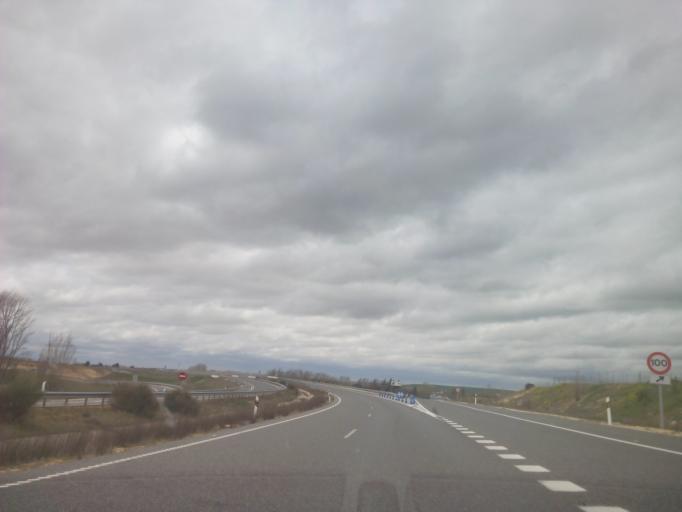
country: ES
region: Castille and Leon
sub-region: Provincia de Salamanca
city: Pelabravo
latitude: 40.9423
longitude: -5.5961
